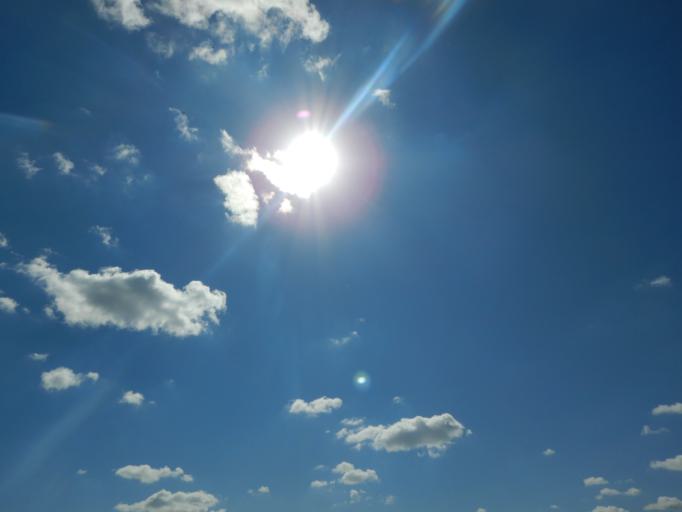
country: AR
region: Santiago del Estero
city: Los Juries
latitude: -28.6659
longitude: -61.5298
